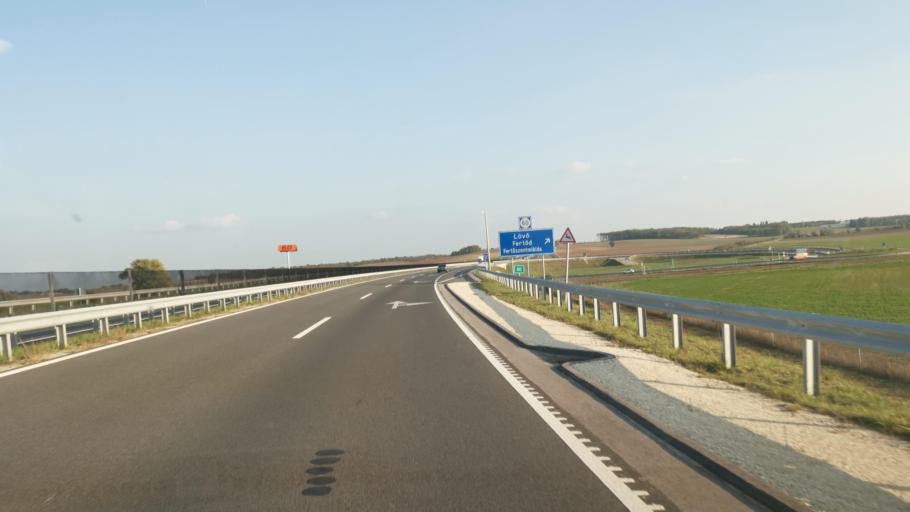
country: HU
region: Gyor-Moson-Sopron
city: Fertoszentmiklos
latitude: 47.5678
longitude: 16.8555
